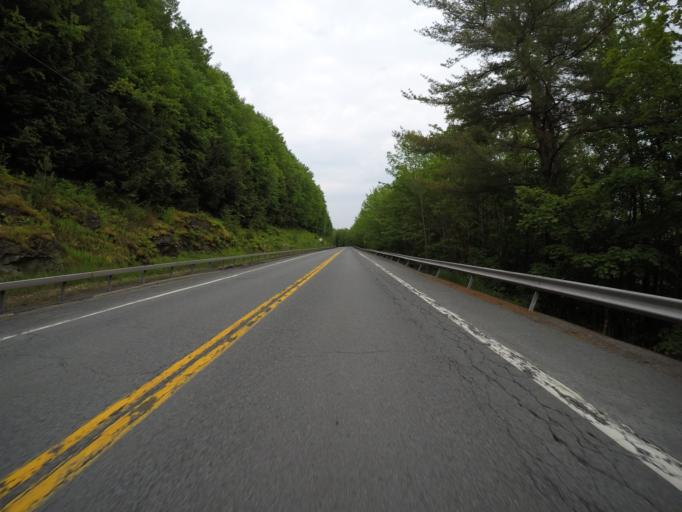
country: US
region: New York
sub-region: Sullivan County
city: Livingston Manor
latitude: 42.0747
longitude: -74.8430
